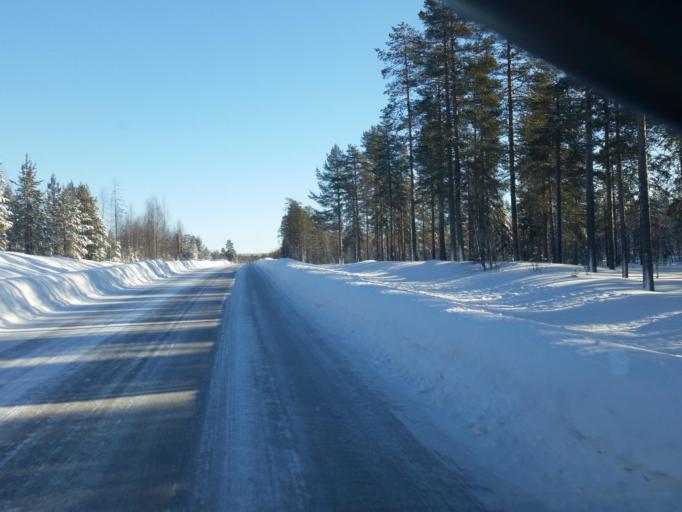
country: SE
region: Vaesterbotten
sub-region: Skelleftea Kommun
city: Storvik
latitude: 65.3288
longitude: 20.6547
